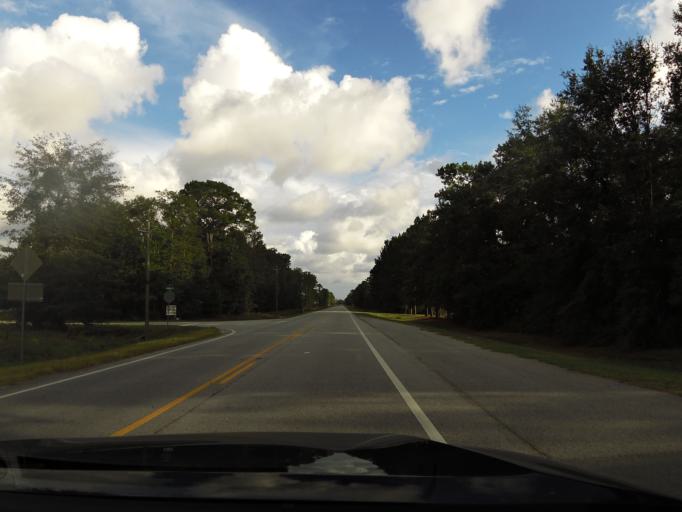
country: US
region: Georgia
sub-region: Liberty County
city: Midway
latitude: 31.7661
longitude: -81.4488
